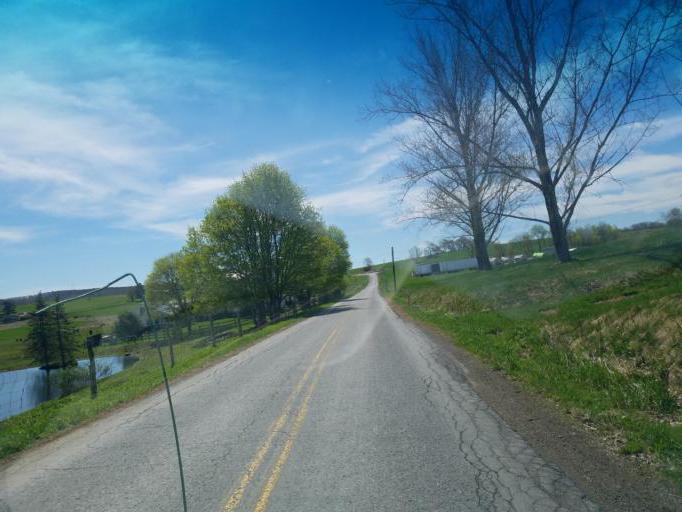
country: US
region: Pennsylvania
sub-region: Potter County
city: Galeton
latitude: 41.8908
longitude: -77.7437
